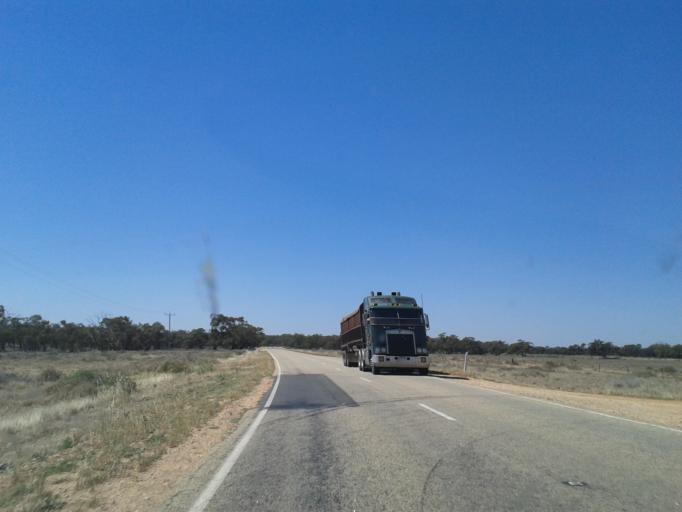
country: AU
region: Victoria
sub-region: Swan Hill
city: Swan Hill
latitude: -34.7636
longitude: 143.2100
